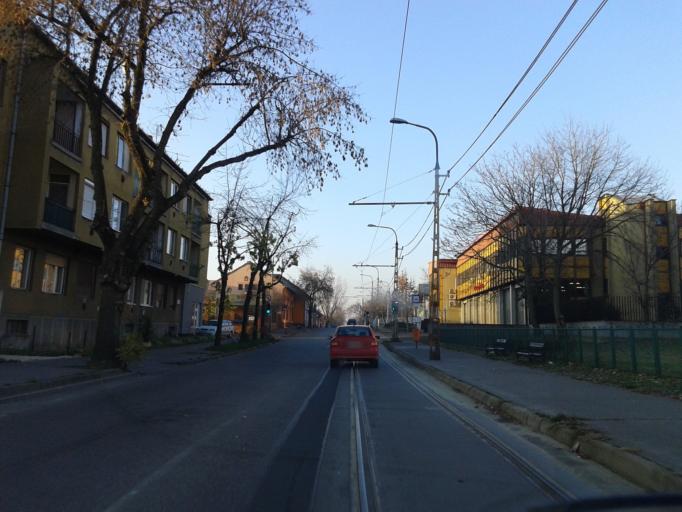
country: HU
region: Budapest
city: Budapest XX. keruelet
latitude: 47.4346
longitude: 19.1071
